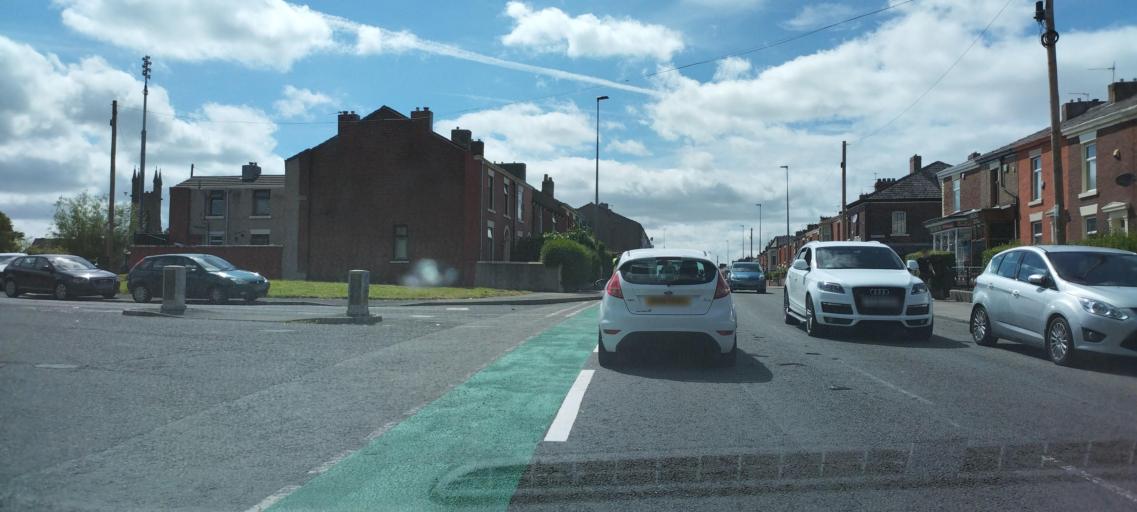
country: GB
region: England
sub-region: Blackburn with Darwen
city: Blackburn
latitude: 53.7426
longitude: -2.5009
